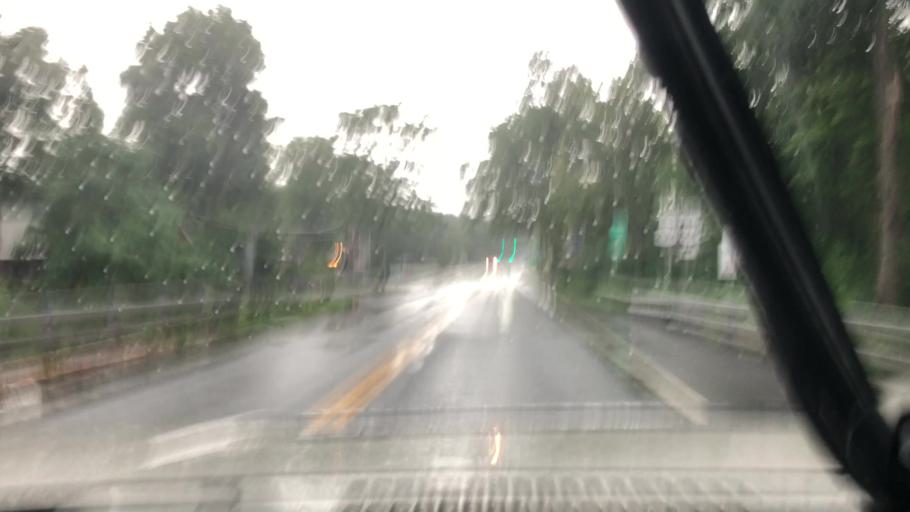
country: US
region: New York
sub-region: Greene County
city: Palenville
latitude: 42.1908
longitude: -73.9856
